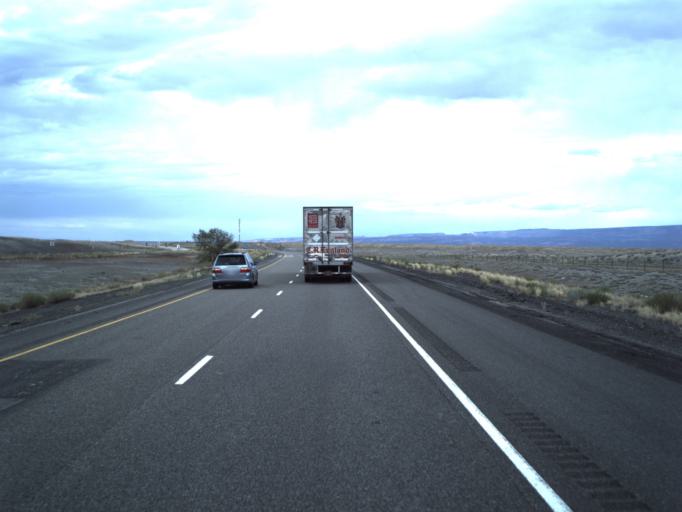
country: US
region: Utah
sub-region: Grand County
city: Moab
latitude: 38.9329
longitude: -109.4239
